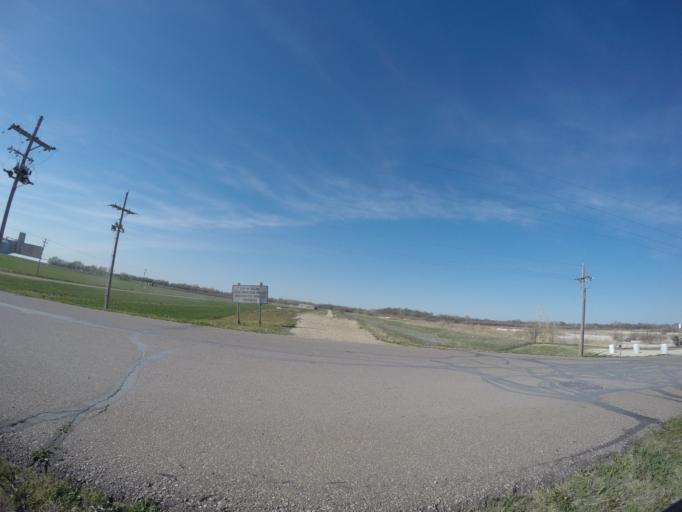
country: US
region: Kansas
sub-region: Saline County
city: Salina
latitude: 38.8525
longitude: -97.5748
